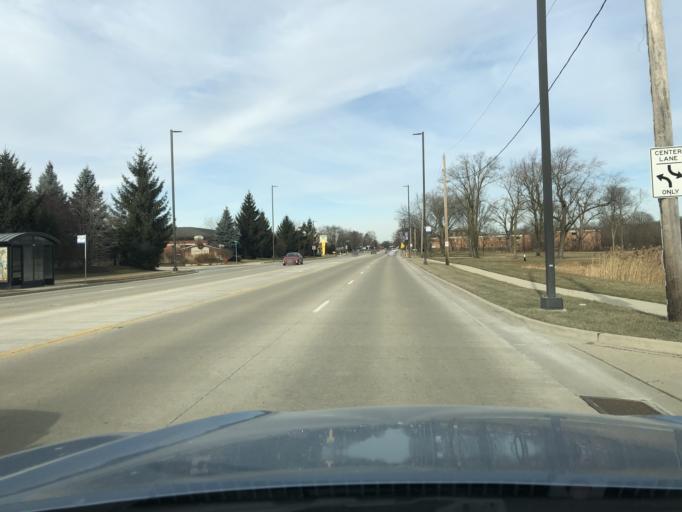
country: US
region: Illinois
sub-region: Cook County
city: Wheeling
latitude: 42.1298
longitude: -87.9000
